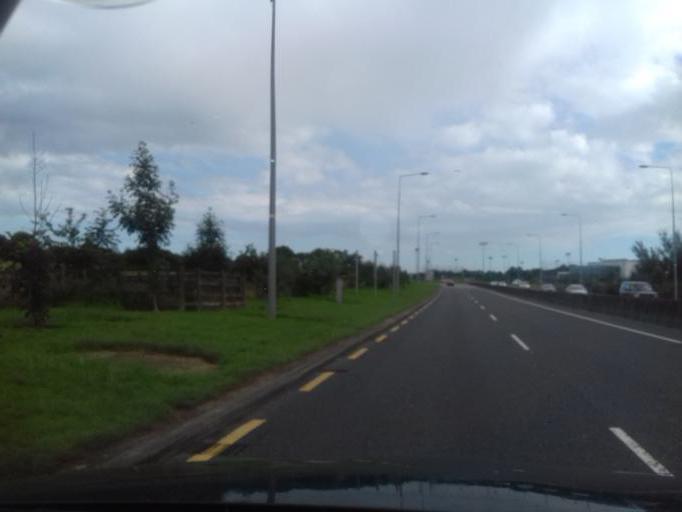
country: IE
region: Munster
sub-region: Waterford
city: Waterford
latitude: 52.2561
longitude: -7.1801
